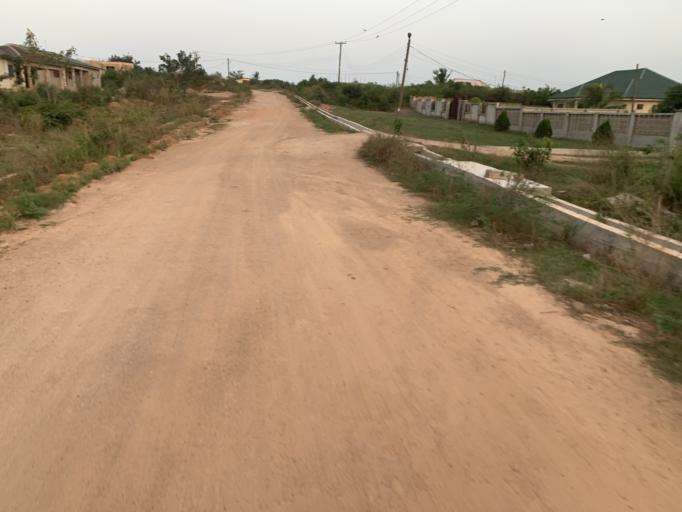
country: GH
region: Central
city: Winneba
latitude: 5.3761
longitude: -0.6090
